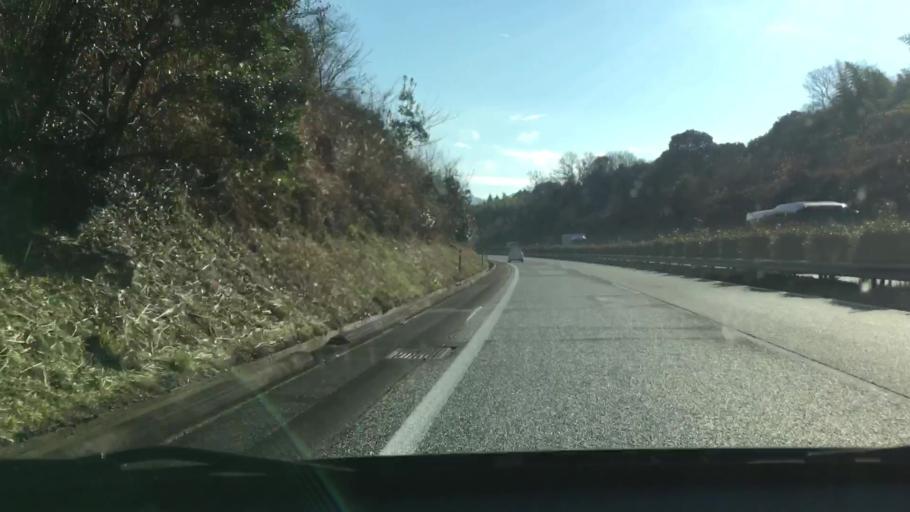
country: JP
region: Kumamoto
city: Hitoyoshi
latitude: 32.1910
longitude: 130.7771
